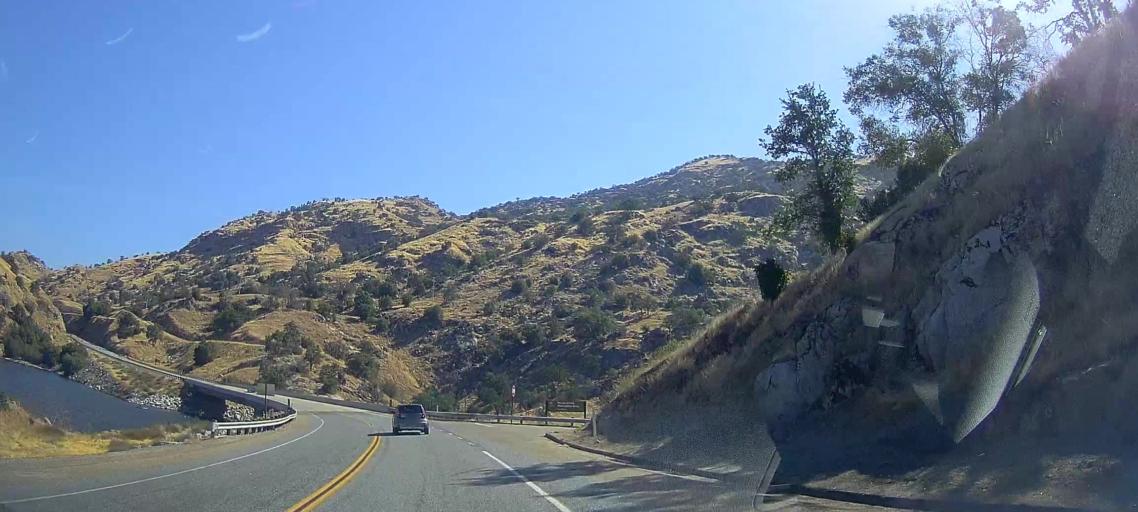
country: US
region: California
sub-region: Tulare County
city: Three Rivers
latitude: 36.3880
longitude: -118.9466
